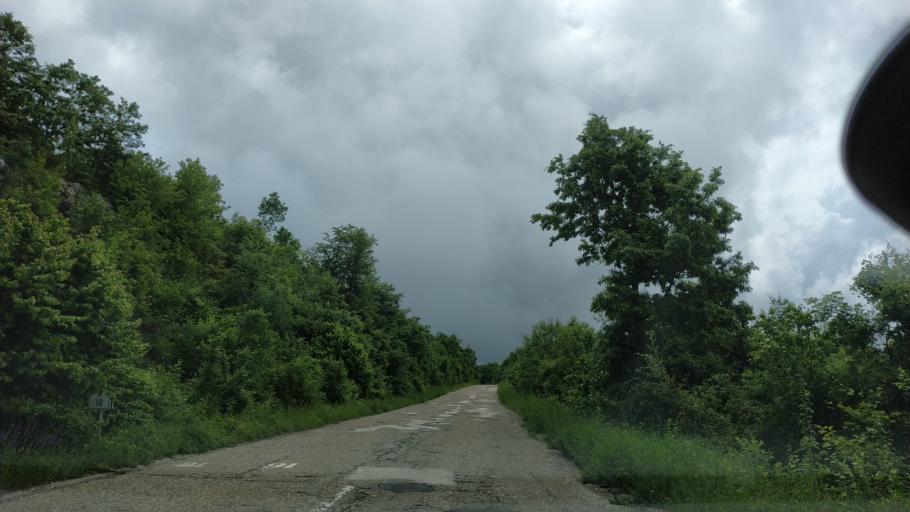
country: RS
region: Central Serbia
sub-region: Zajecarski Okrug
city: Boljevac
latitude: 43.7236
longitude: 21.9475
